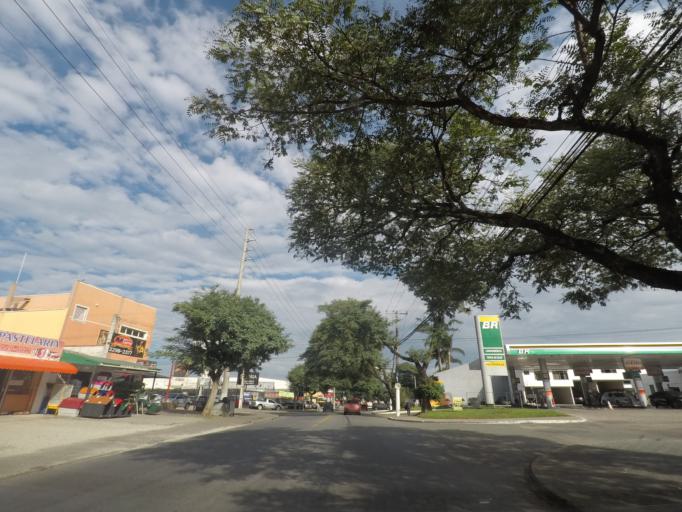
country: BR
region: Parana
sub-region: Sao Jose Dos Pinhais
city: Sao Jose dos Pinhais
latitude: -25.5360
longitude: -49.2954
